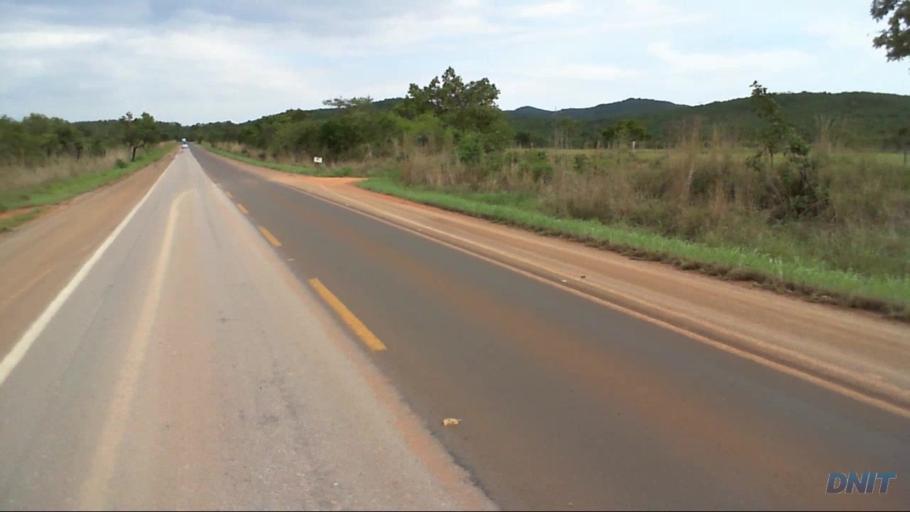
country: BR
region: Goias
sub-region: Barro Alto
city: Barro Alto
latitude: -14.9466
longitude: -48.9352
